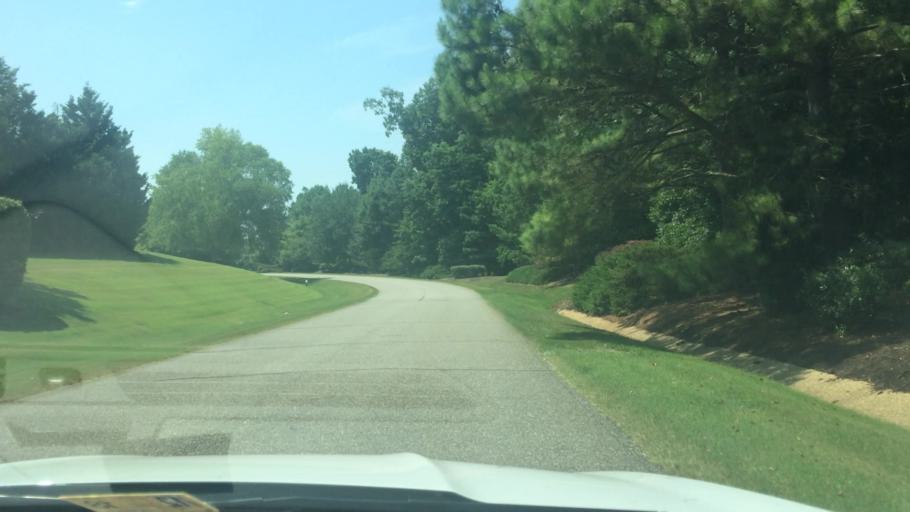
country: US
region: Virginia
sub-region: City of Williamsburg
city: Williamsburg
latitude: 37.2232
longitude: -76.6541
